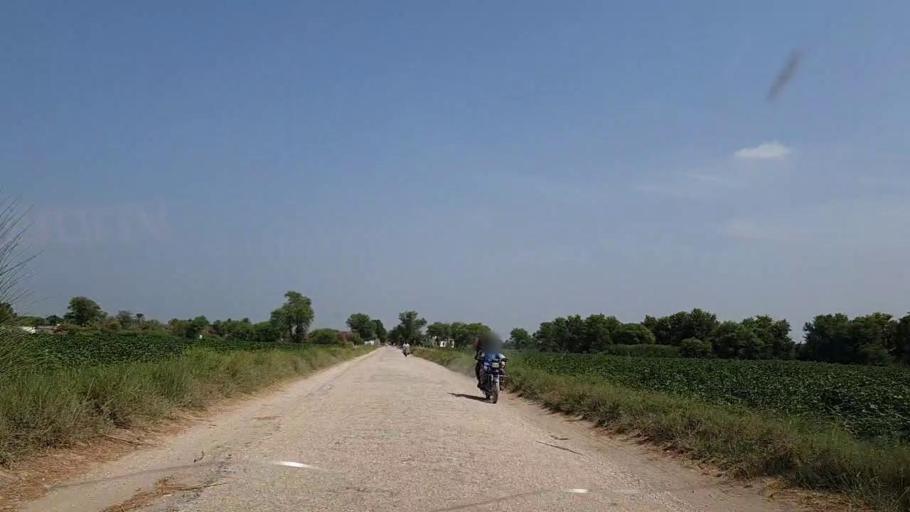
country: PK
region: Sindh
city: Adilpur
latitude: 27.8293
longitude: 69.2939
